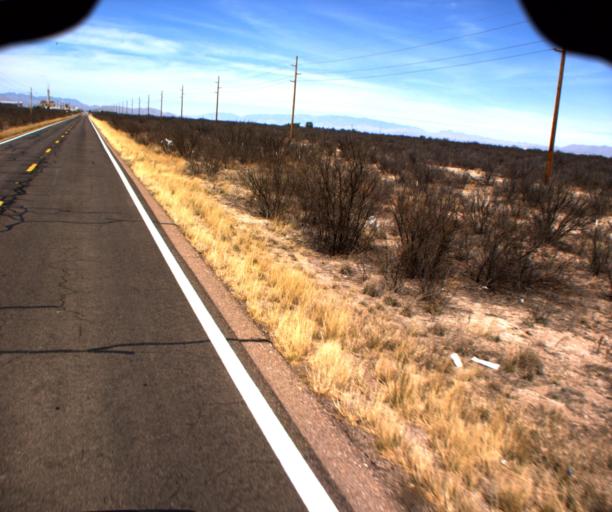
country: US
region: Arizona
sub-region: Cochise County
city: Willcox
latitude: 32.0278
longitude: -109.8748
